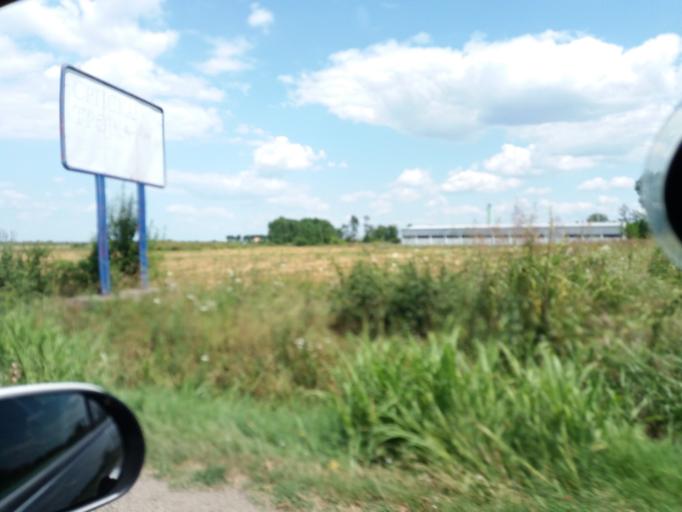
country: RS
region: Autonomna Pokrajina Vojvodina
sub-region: Sremski Okrug
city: Pecinci
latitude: 44.8621
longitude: 19.9599
